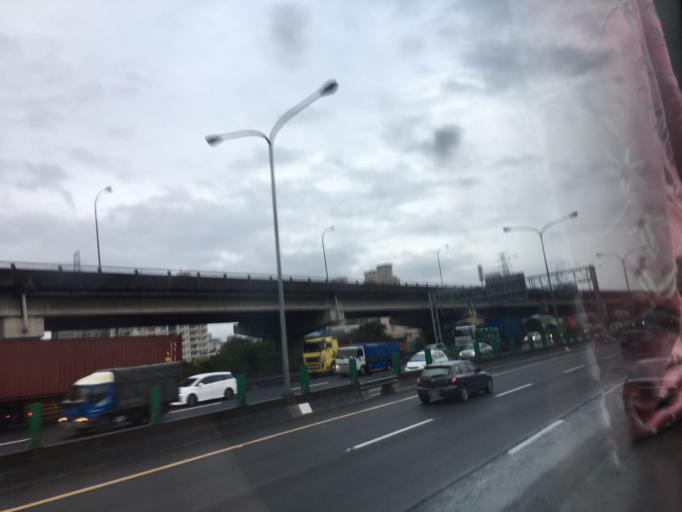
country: TW
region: Taipei
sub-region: Taipei
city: Banqiao
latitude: 25.0757
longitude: 121.4648
